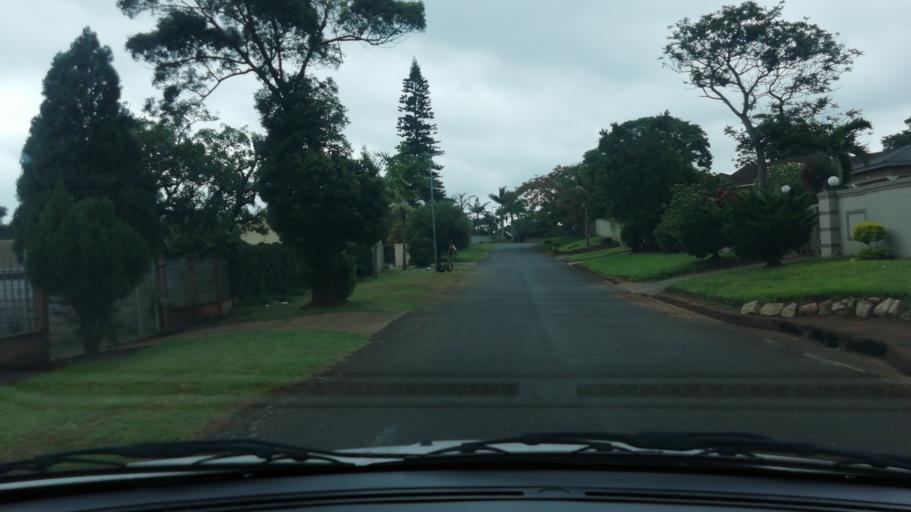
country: ZA
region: KwaZulu-Natal
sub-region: uThungulu District Municipality
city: Empangeni
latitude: -28.7671
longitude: 31.8997
